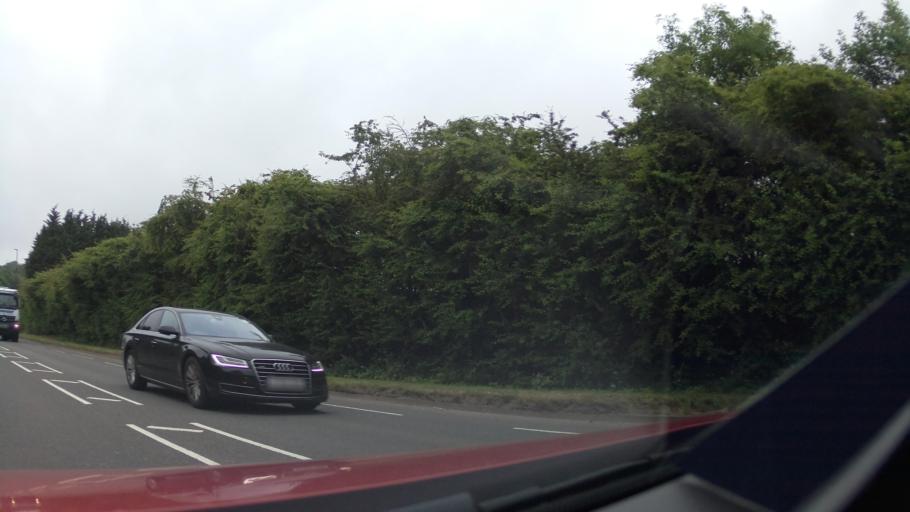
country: GB
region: England
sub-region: Derbyshire
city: Swadlincote
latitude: 52.7703
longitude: -1.5951
